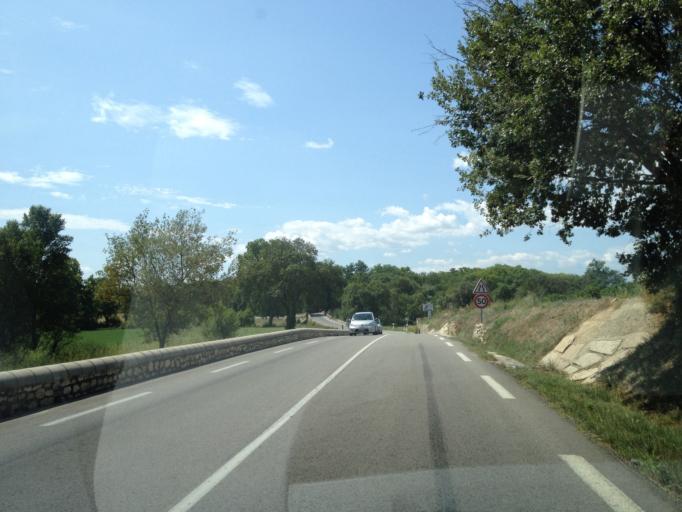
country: FR
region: Languedoc-Roussillon
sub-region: Departement du Gard
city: Villevieille
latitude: 43.8139
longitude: 4.0953
